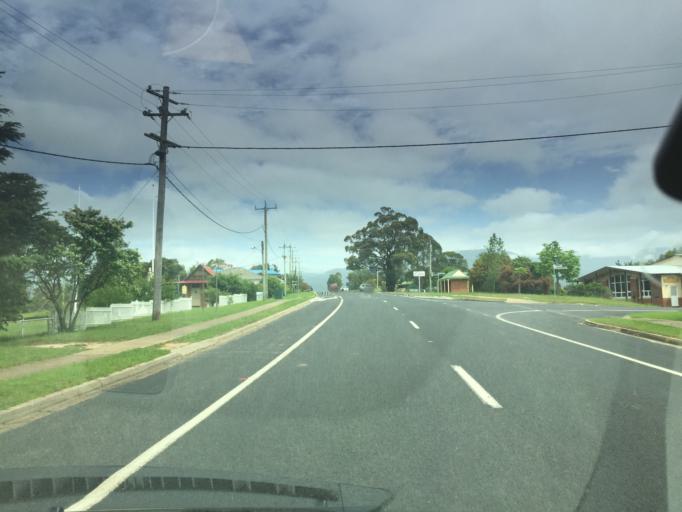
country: AU
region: New South Wales
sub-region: Bega Valley
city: Bega
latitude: -36.6269
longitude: 149.5683
